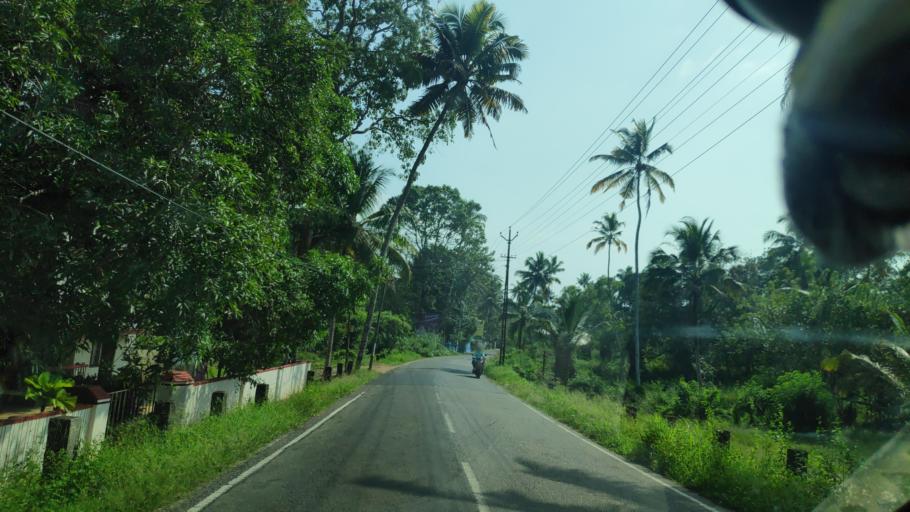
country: IN
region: Kerala
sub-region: Alappuzha
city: Shertallai
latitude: 9.6238
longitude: 76.3006
